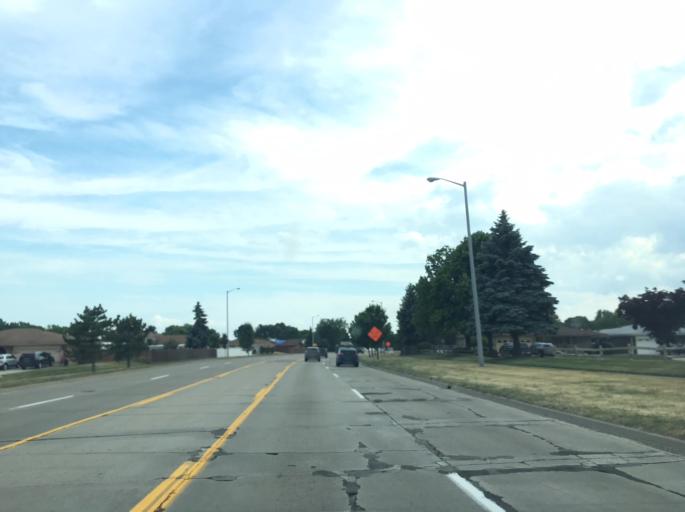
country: US
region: Michigan
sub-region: Macomb County
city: Fraser
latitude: 42.5589
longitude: -82.9877
